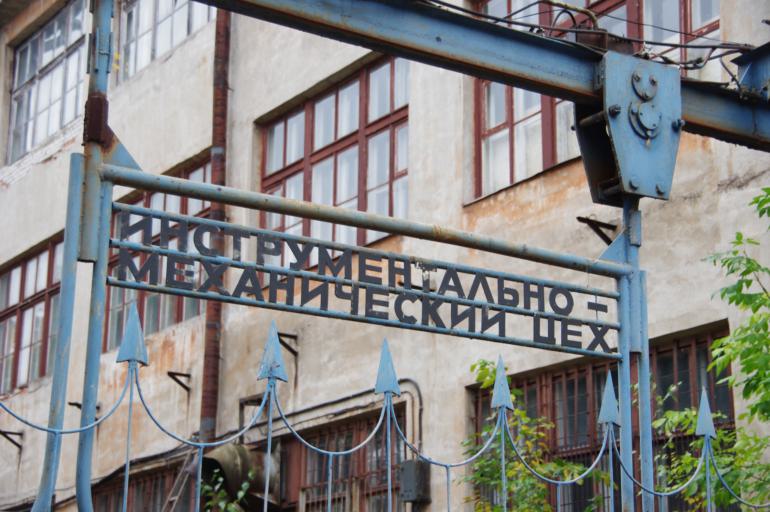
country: RU
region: St.-Petersburg
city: Kronshtadt
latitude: 59.9899
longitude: 29.7713
